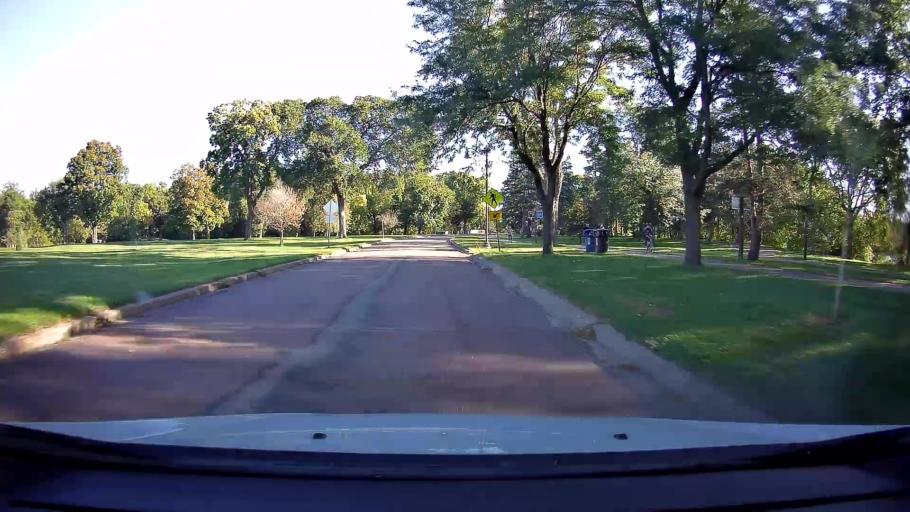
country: US
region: Minnesota
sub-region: Hennepin County
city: Richfield
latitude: 44.9139
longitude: -93.2431
